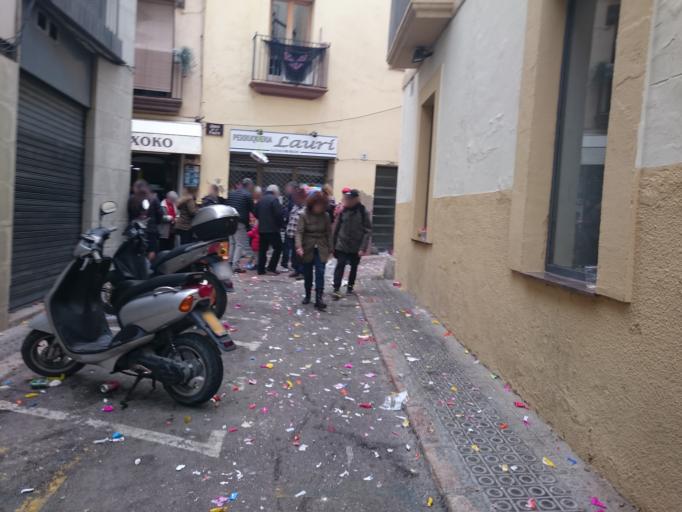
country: ES
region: Catalonia
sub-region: Provincia de Barcelona
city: Vilanova i la Geltru
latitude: 41.2248
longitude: 1.7268
